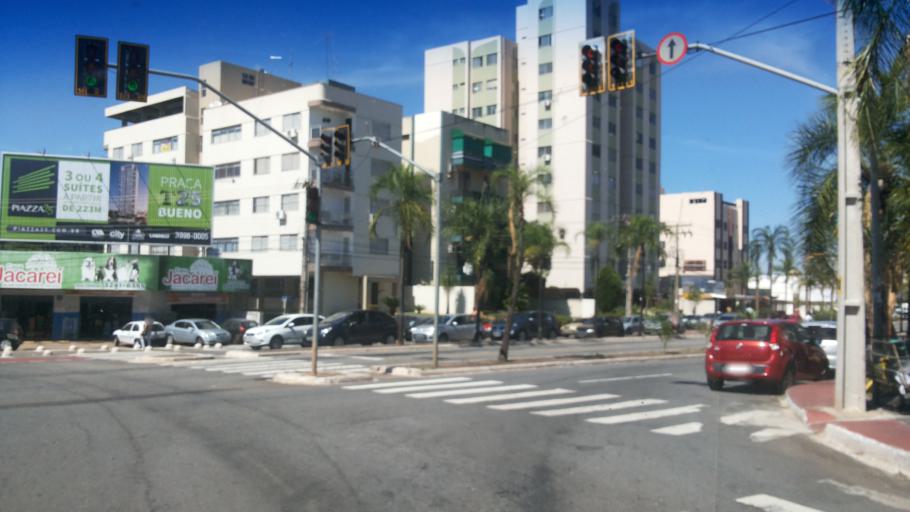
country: BR
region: Goias
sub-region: Goiania
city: Goiania
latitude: -16.6980
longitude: -49.2526
